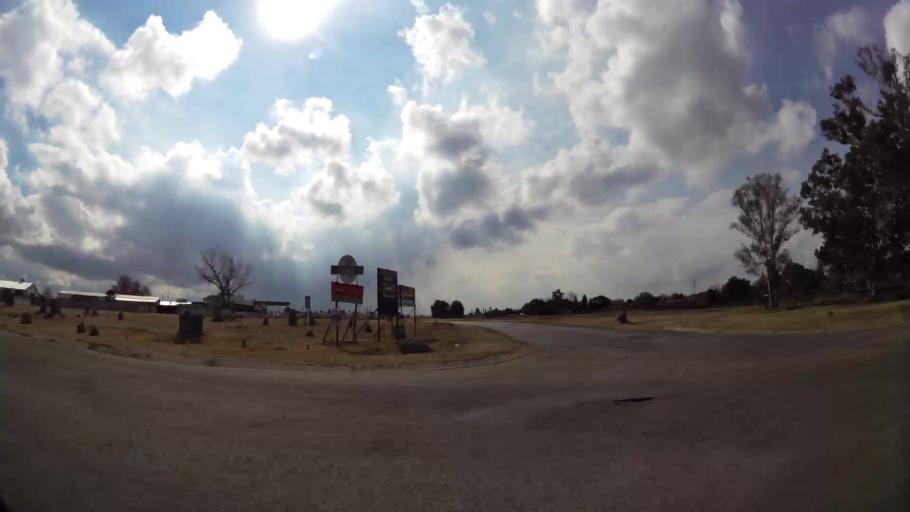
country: ZA
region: Gauteng
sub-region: Sedibeng District Municipality
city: Vanderbijlpark
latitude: -26.7402
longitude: 27.8222
